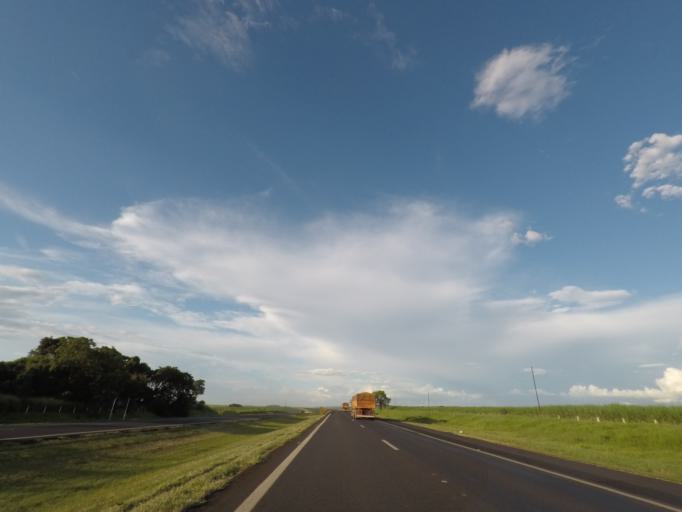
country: BR
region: Sao Paulo
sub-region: Ituverava
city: Ituverava
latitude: -20.3027
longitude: -47.7999
